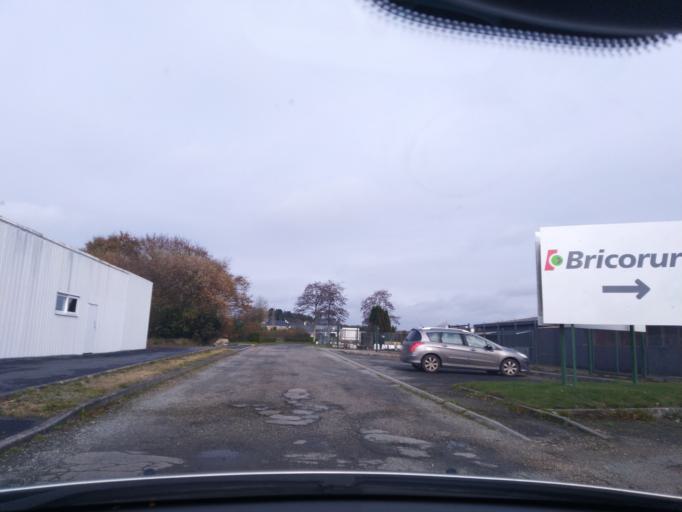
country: FR
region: Brittany
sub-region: Departement du Finistere
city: Guerlesquin
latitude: 48.5153
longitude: -3.5856
